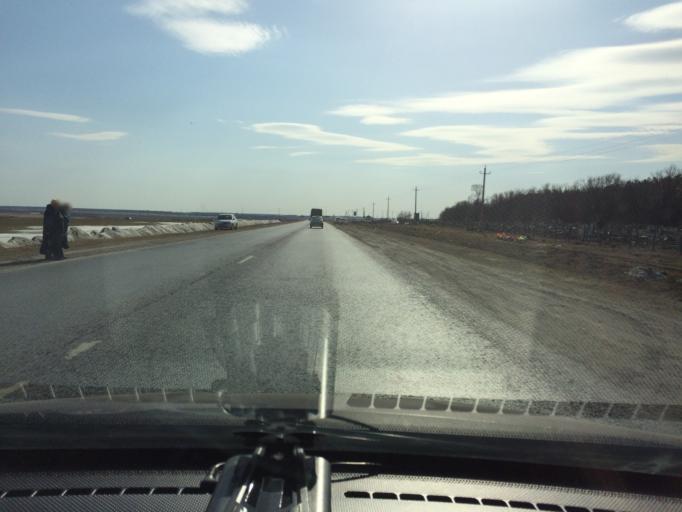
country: RU
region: Mariy-El
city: Yoshkar-Ola
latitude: 56.7002
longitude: 48.0671
